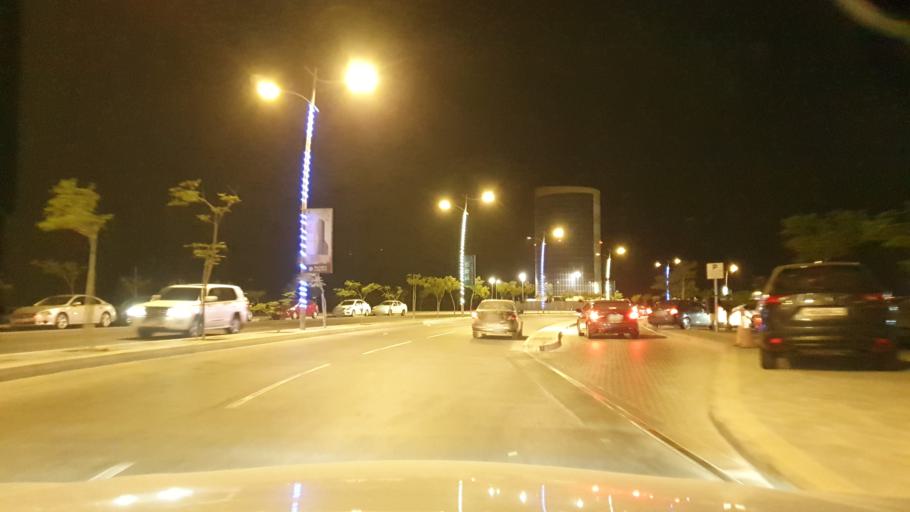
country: BH
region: Manama
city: Jidd Hafs
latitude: 26.2415
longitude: 50.5524
